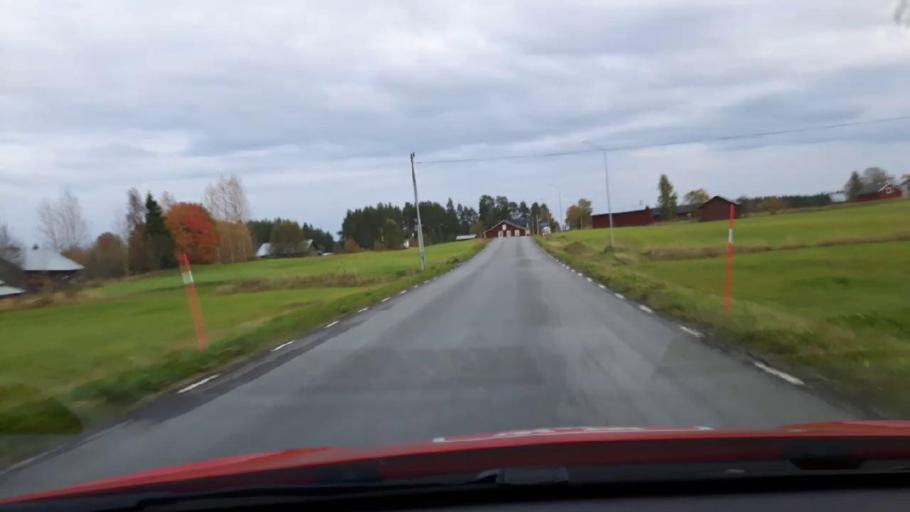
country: SE
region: Jaemtland
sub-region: OEstersunds Kommun
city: Lit
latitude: 63.3119
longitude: 14.9924
